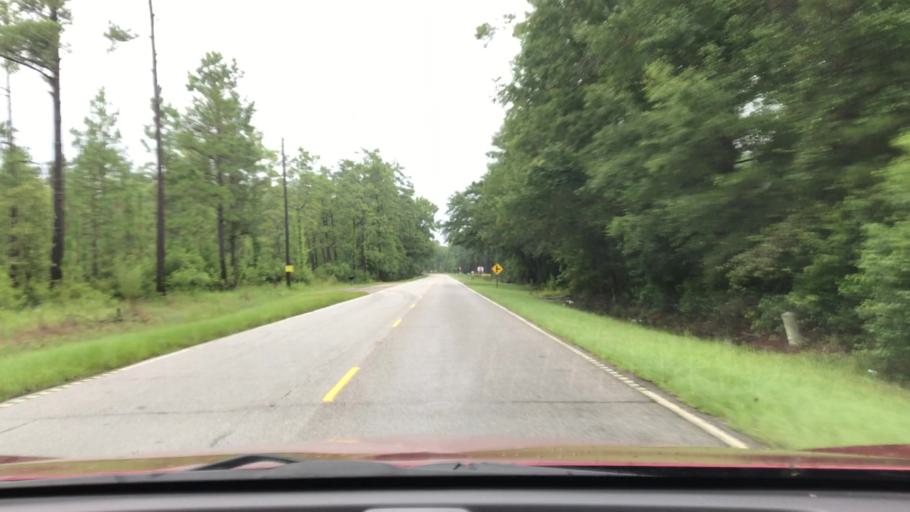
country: US
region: South Carolina
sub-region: Georgetown County
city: Murrells Inlet
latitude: 33.6089
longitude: -79.1978
